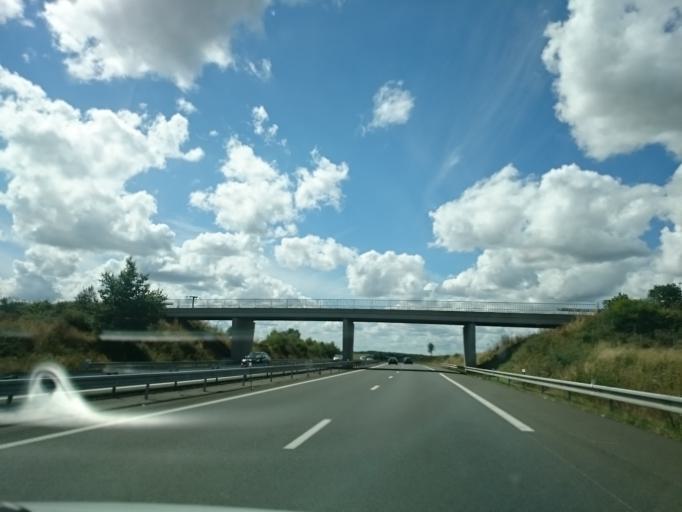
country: FR
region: Pays de la Loire
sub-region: Departement de Maine-et-Loire
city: Saint-Germain-des-Pres
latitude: 47.4377
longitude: -0.8404
